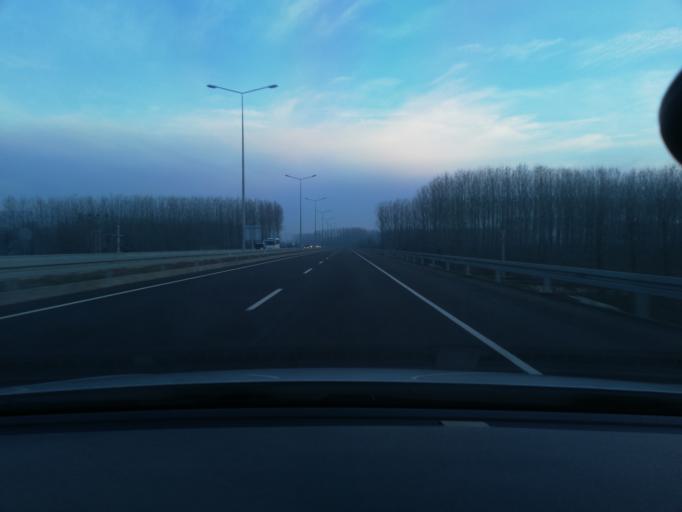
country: TR
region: Duzce
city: Duzce
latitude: 40.8068
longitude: 31.1687
